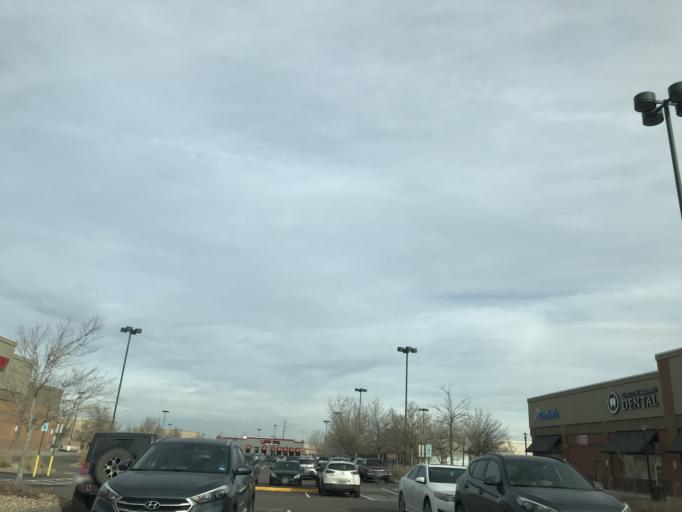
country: US
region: Colorado
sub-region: Adams County
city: Commerce City
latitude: 39.7656
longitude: -104.9011
